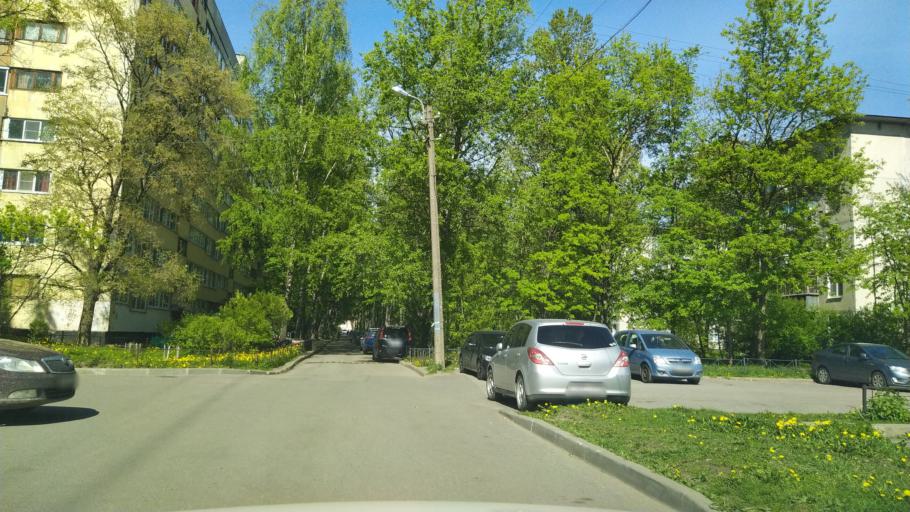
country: RU
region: St.-Petersburg
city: Grazhdanka
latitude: 60.0387
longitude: 30.4188
